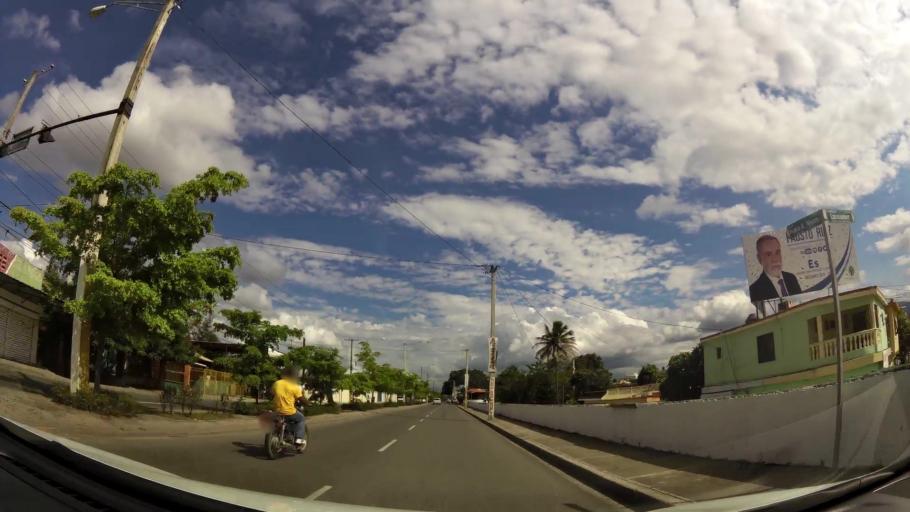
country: DO
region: La Vega
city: Concepcion de La Vega
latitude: 19.2285
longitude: -70.5261
